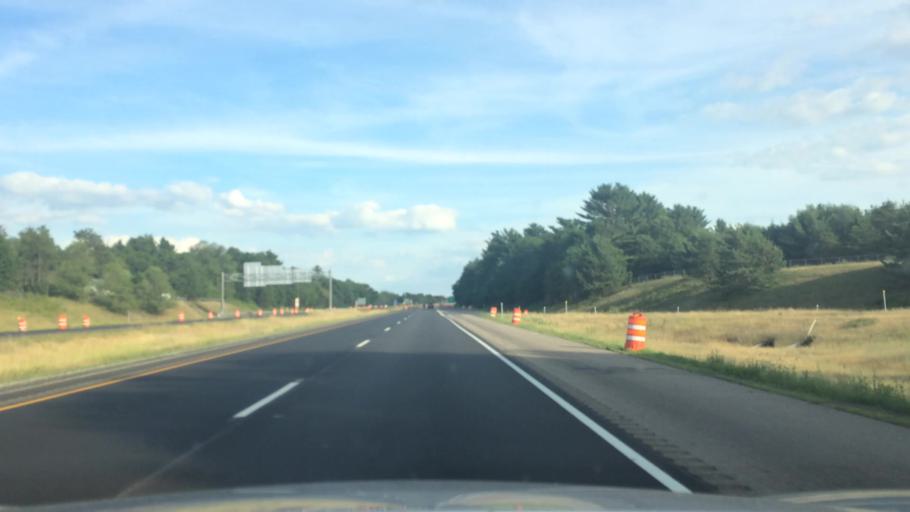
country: US
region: Wisconsin
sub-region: Portage County
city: Whiting
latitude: 44.5217
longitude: -89.5260
